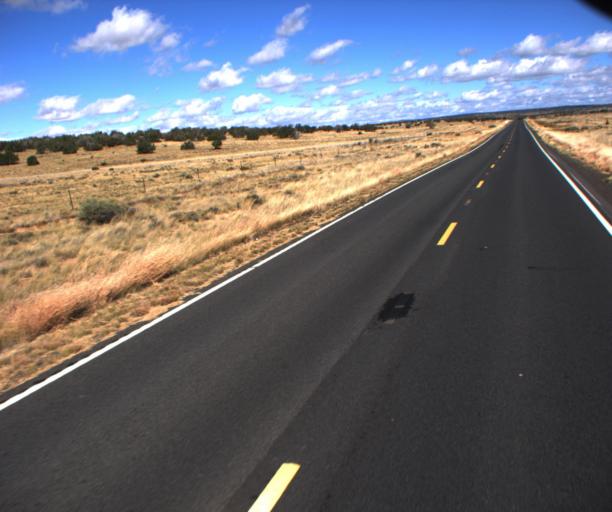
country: US
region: Arizona
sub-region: Apache County
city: Houck
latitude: 34.9908
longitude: -109.2271
